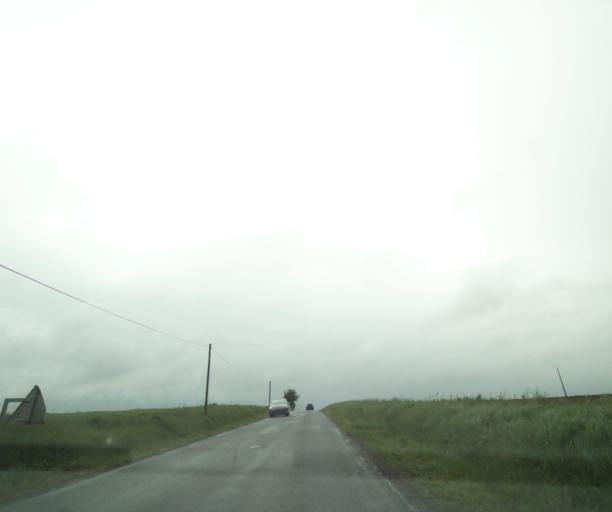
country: FR
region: Poitou-Charentes
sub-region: Departement de la Charente-Maritime
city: Corme-Royal
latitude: 45.7116
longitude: -0.8017
